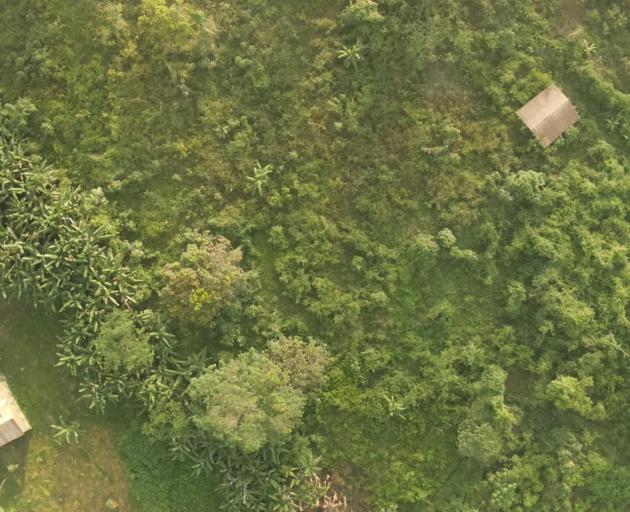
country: BO
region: La Paz
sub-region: Provincia Larecaja
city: Guanay
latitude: -15.7731
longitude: -67.6592
